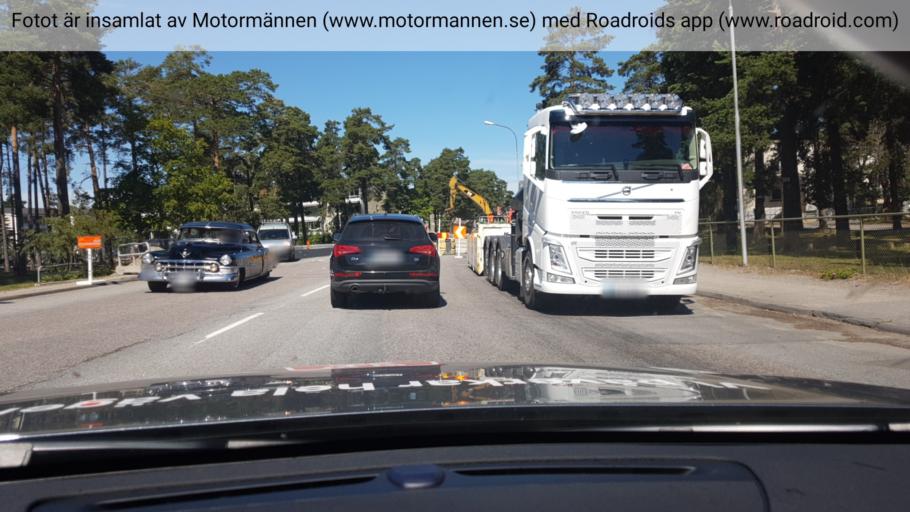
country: SE
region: Stockholm
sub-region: Haninge Kommun
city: Haninge
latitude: 59.1686
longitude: 18.1493
